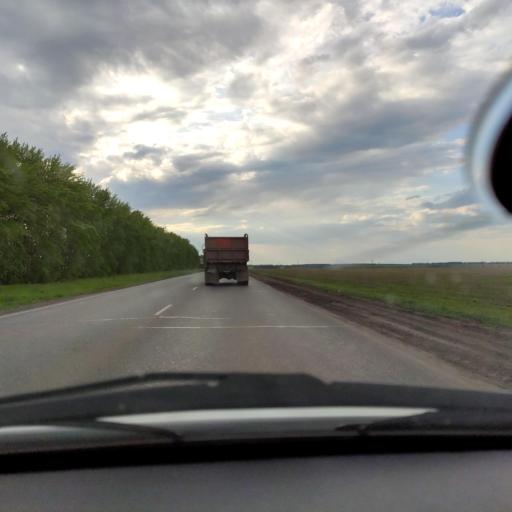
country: RU
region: Bashkortostan
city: Dyurtyuli
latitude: 55.3867
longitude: 54.8536
